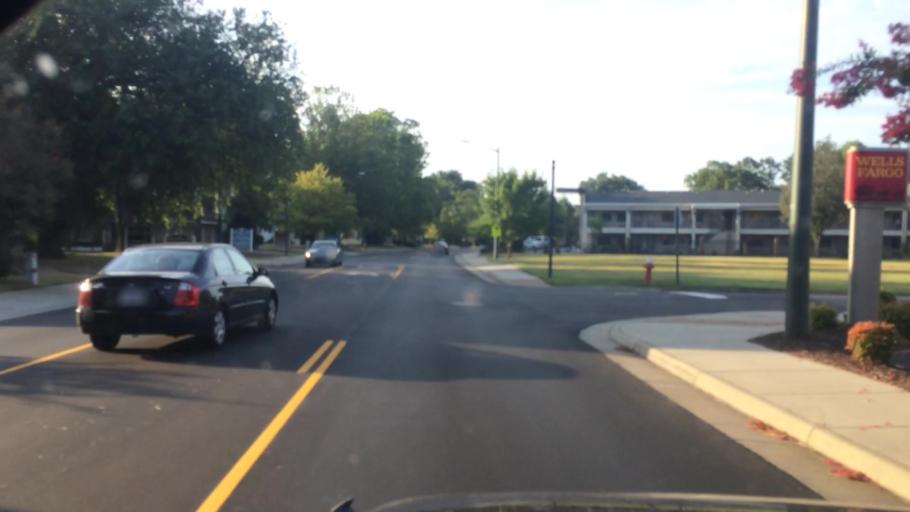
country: US
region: Virginia
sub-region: City of Williamsburg
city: Williamsburg
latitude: 37.2796
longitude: -76.7176
